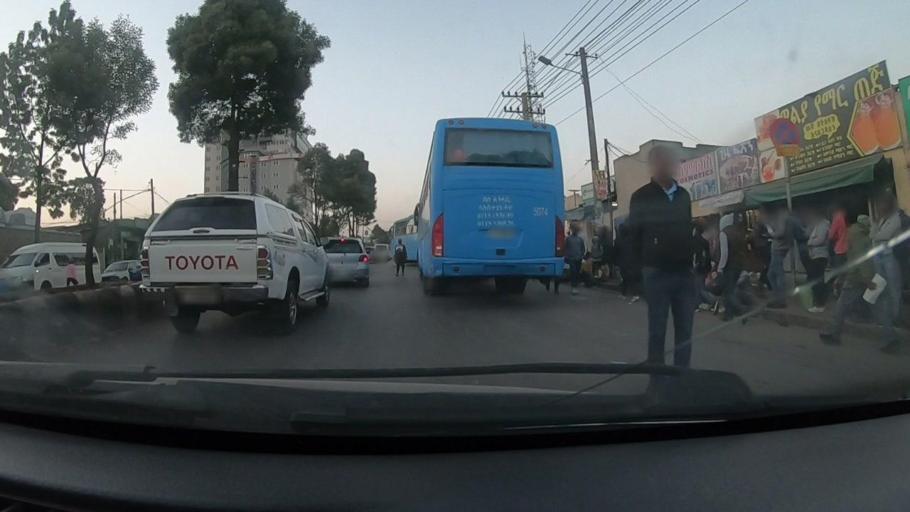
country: ET
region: Adis Abeba
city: Addis Ababa
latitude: 9.0388
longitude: 38.7517
